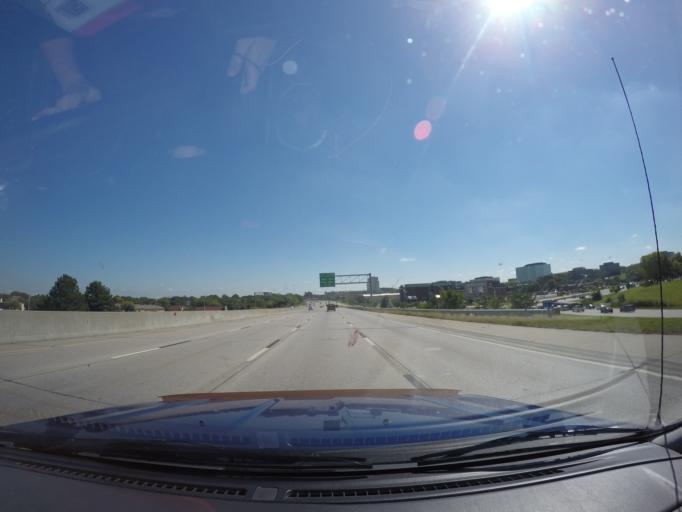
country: US
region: Kansas
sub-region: Johnson County
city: Overland Park
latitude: 38.9322
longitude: -94.6689
